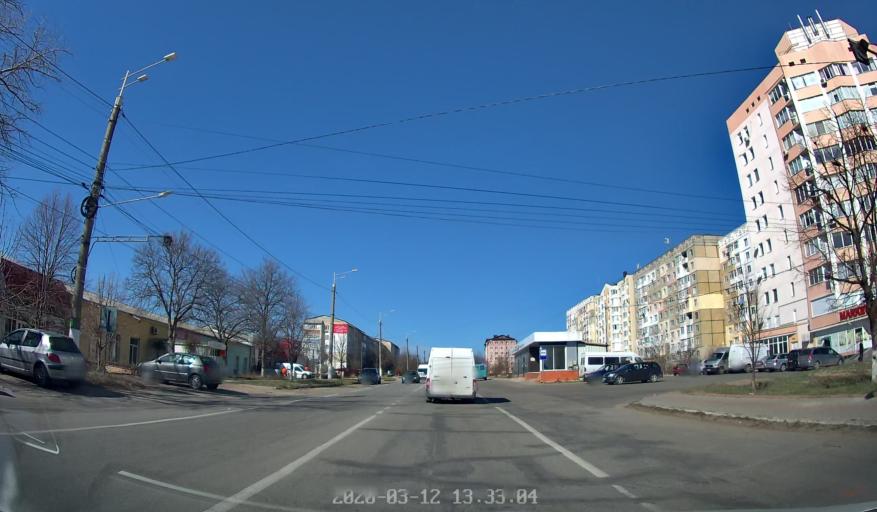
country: MD
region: Laloveni
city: Ialoveni
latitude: 46.9546
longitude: 28.7699
